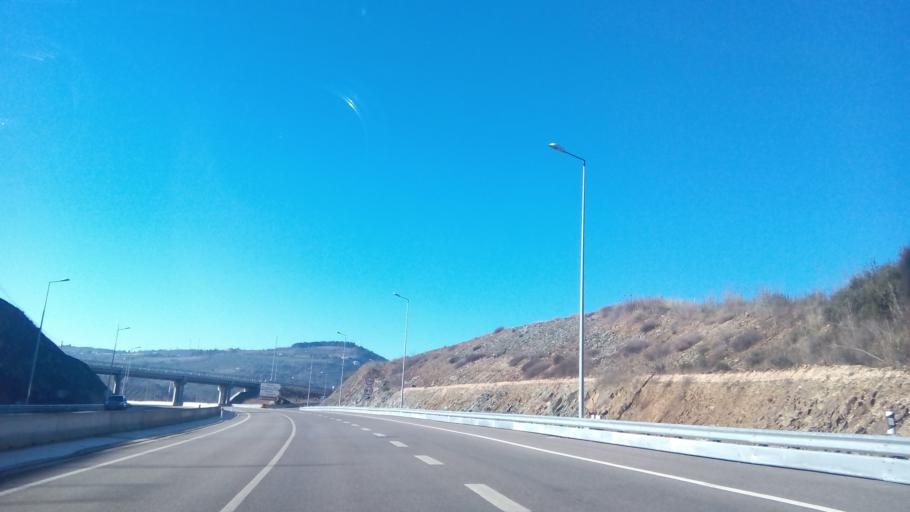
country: PT
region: Braganca
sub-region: Braganca Municipality
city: Braganca
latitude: 41.7917
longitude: -6.7183
